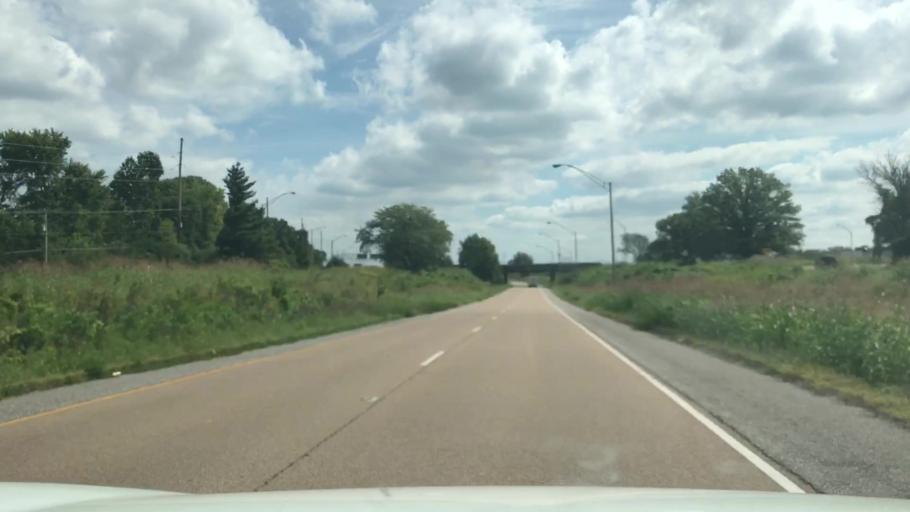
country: US
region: Illinois
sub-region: Saint Clair County
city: Alorton
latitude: 38.5478
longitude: -90.0644
